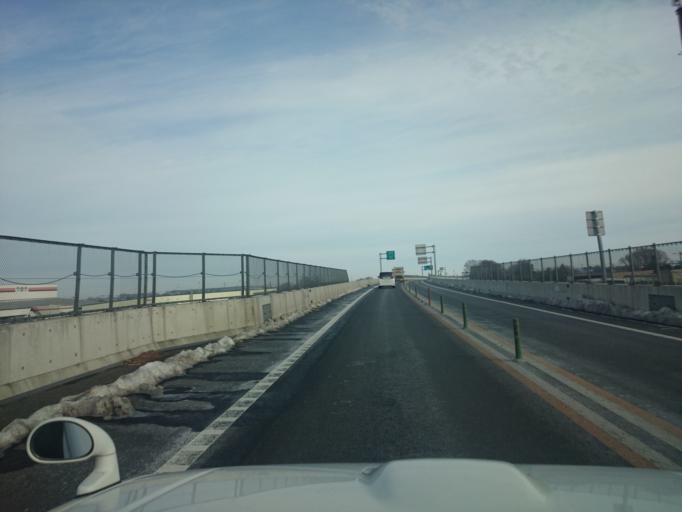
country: JP
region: Saitama
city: Satte
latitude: 36.0818
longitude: 139.7561
